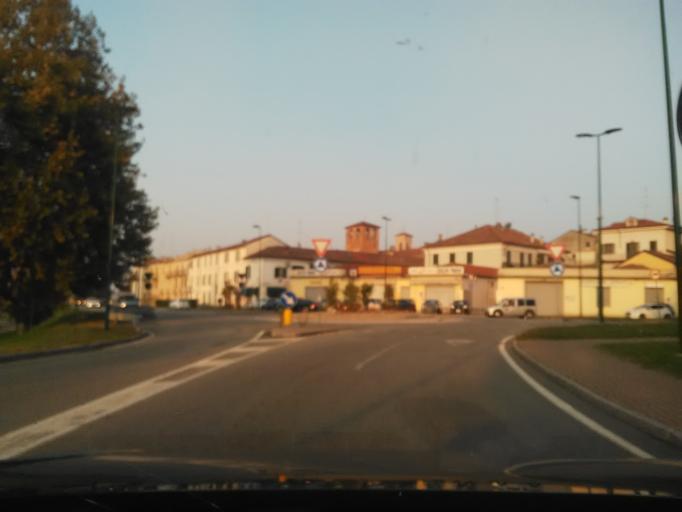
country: IT
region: Piedmont
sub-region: Provincia di Alessandria
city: Casale Monferrato
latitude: 45.1386
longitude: 8.4461
